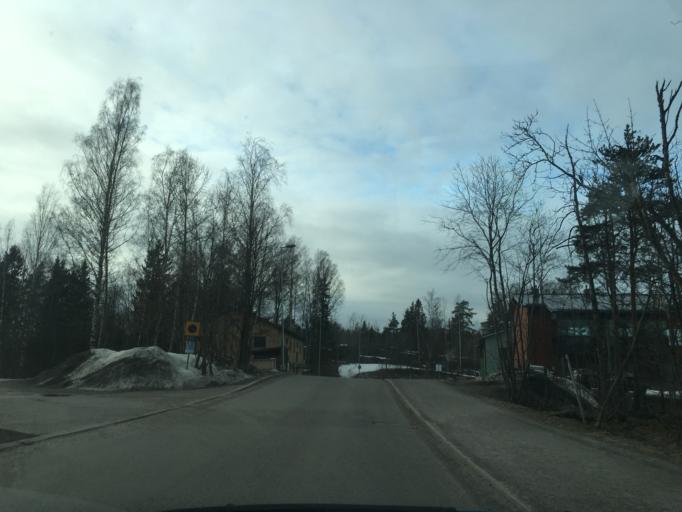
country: FI
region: Uusimaa
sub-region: Helsinki
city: Vantaa
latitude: 60.2626
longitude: 25.0889
